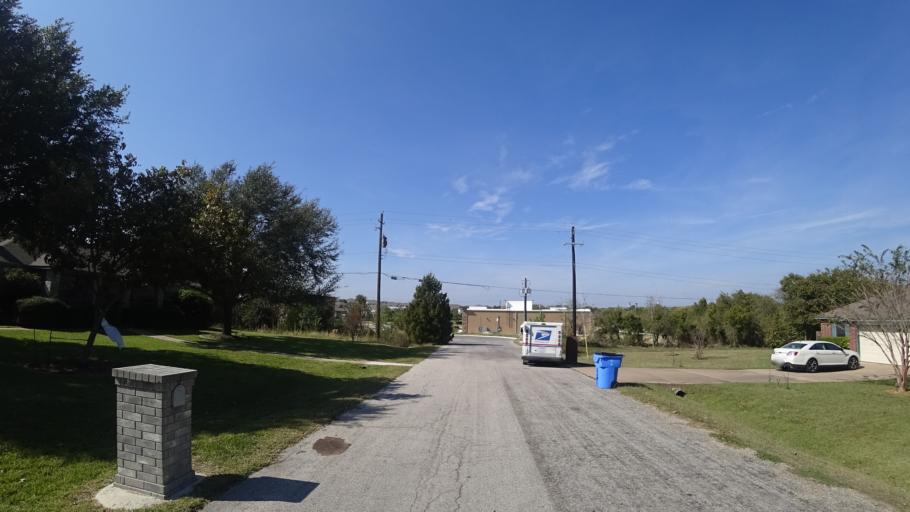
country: US
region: Texas
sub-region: Travis County
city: Pflugerville
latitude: 30.4205
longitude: -97.6272
